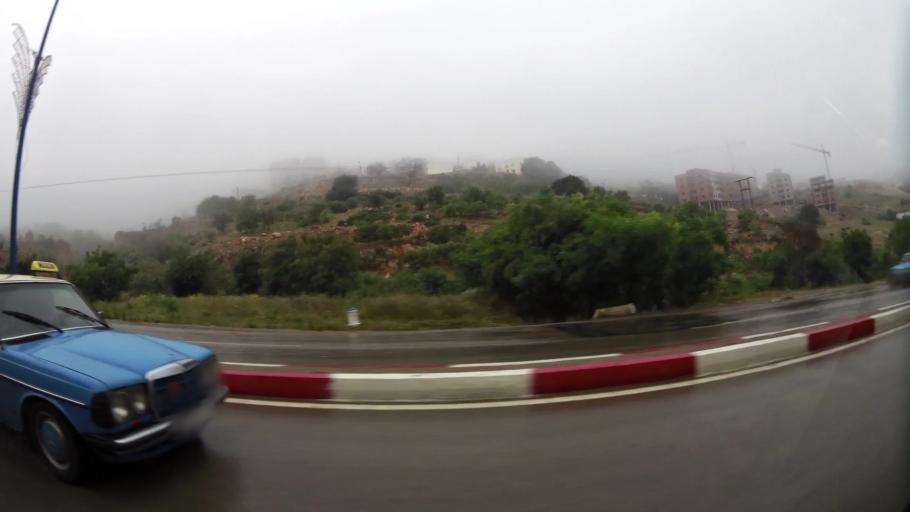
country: MA
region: Taza-Al Hoceima-Taounate
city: Tirhanimine
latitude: 35.2254
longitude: -3.9301
